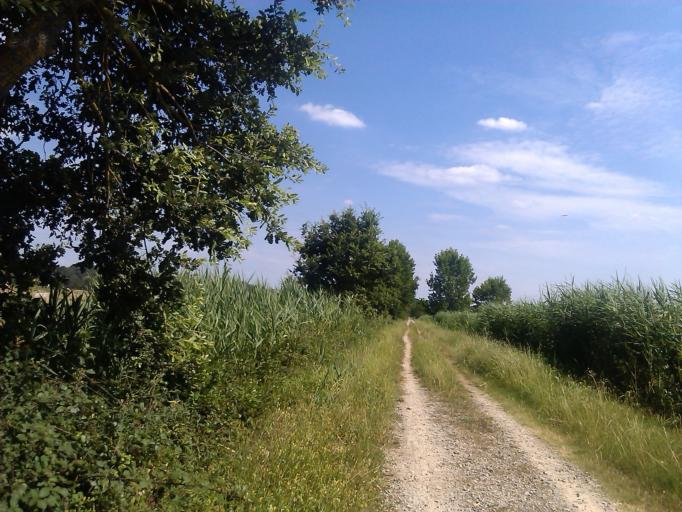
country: IT
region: Tuscany
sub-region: Provincia di Siena
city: Chiusi
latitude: 43.0672
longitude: 11.9294
